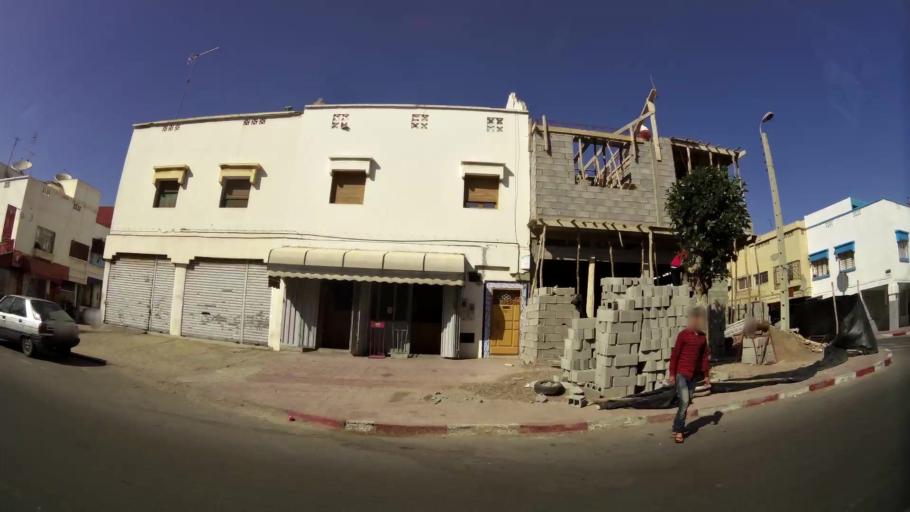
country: MA
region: Oued ed Dahab-Lagouira
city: Dakhla
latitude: 30.4249
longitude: -9.5657
